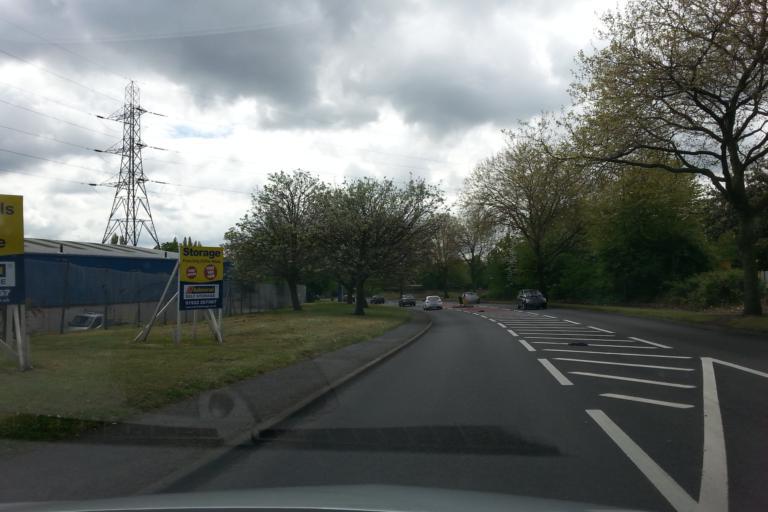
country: GB
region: England
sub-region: Walsall
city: Walsall
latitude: 52.5895
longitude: -2.0133
